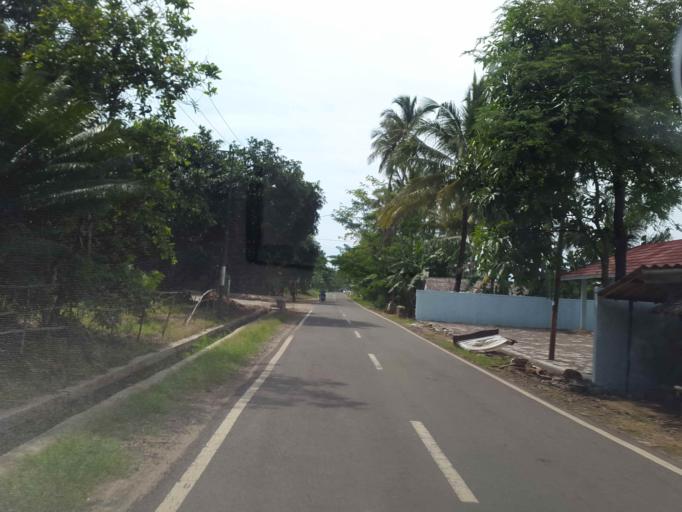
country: ID
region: Banten
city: Citeureup
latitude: -6.5246
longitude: 105.6935
